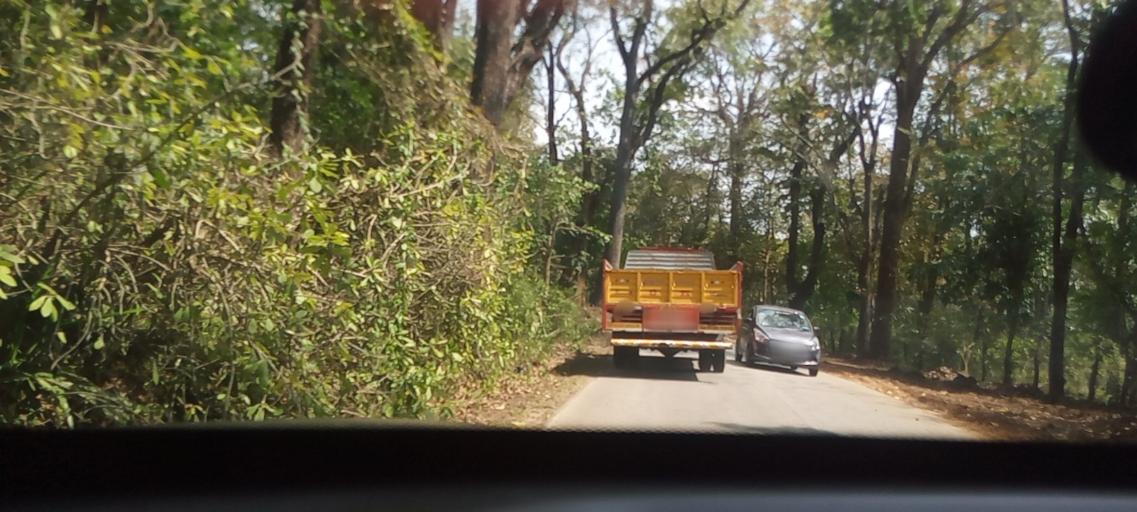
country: IN
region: Karnataka
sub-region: Chikmagalur
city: Mudigere
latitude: 13.3125
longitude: 75.5758
